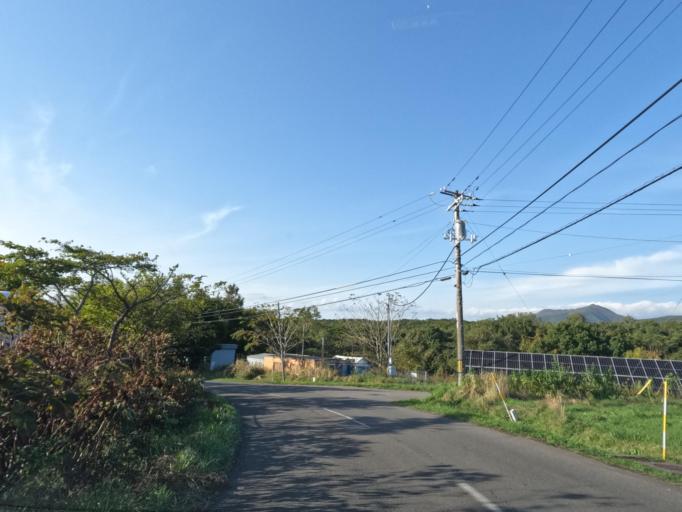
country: JP
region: Hokkaido
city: Muroran
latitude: 42.3970
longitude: 140.9345
